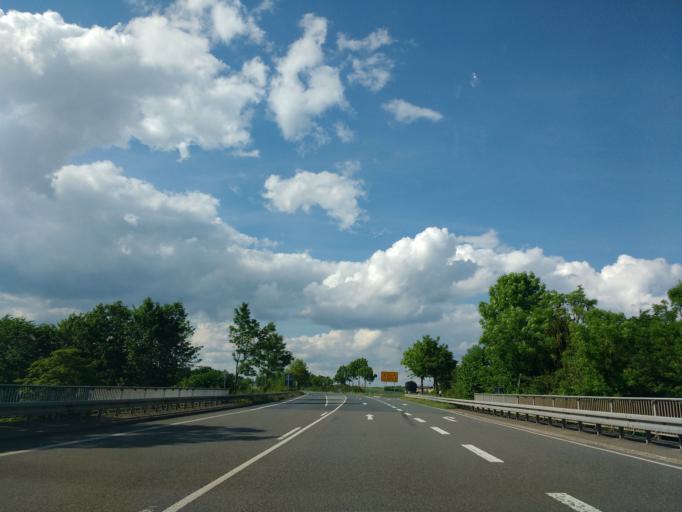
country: DE
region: Hesse
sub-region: Regierungsbezirk Kassel
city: Korbach
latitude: 51.2606
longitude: 8.9058
